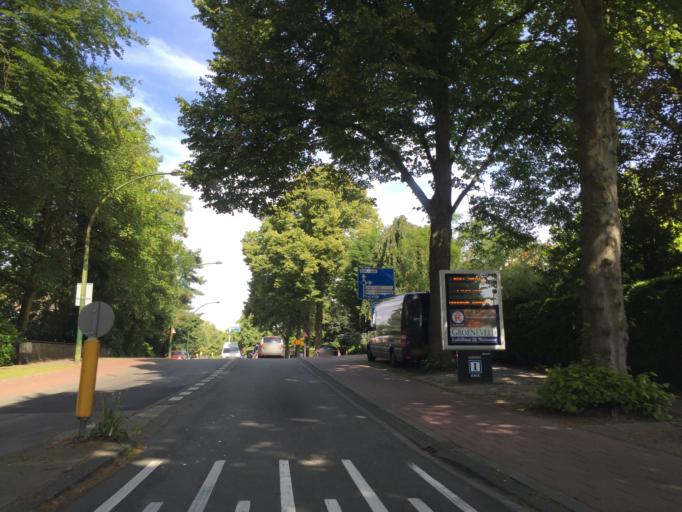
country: NL
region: South Holland
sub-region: Gemeente Wassenaar
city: Wassenaar
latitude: 52.1409
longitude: 4.4010
